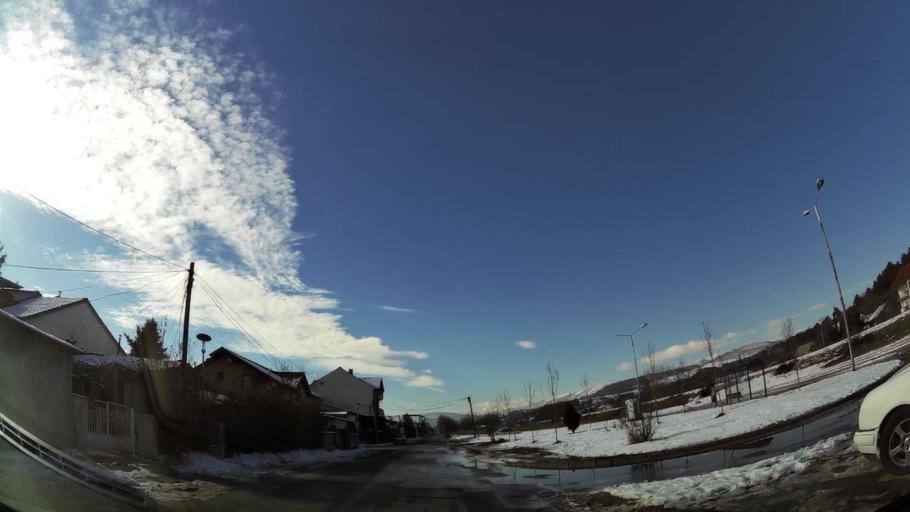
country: MK
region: Saraj
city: Saraj
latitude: 42.0103
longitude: 21.3403
